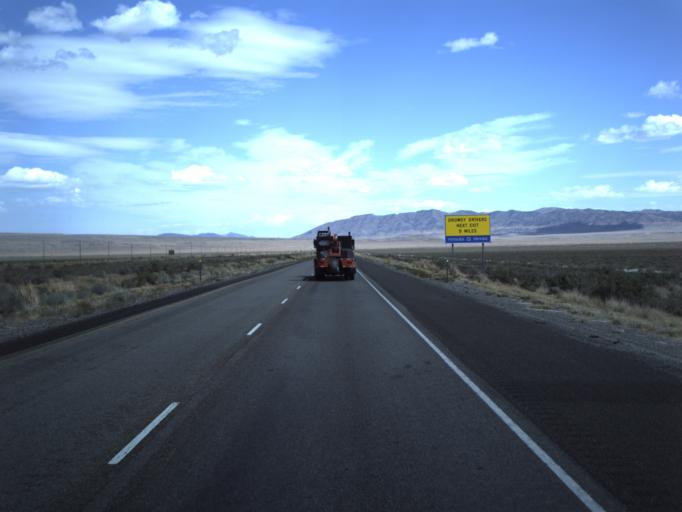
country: US
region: Utah
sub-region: Tooele County
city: Grantsville
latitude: 40.7369
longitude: -113.0941
